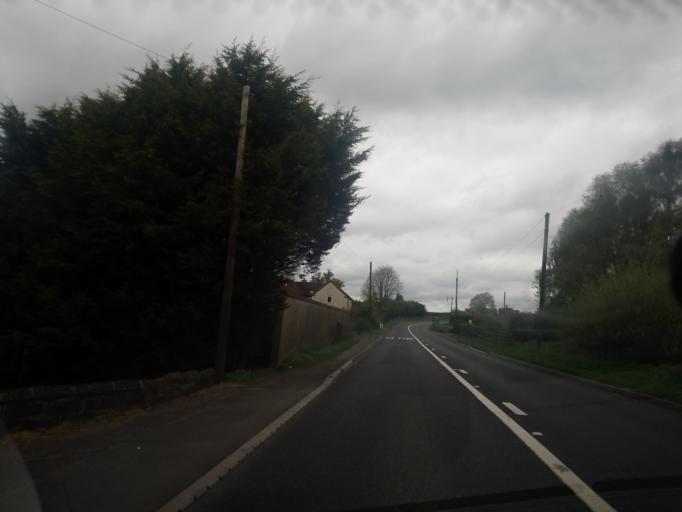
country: GB
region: England
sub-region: Shropshire
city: Stoke upon Tern
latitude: 52.8524
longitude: -2.4807
